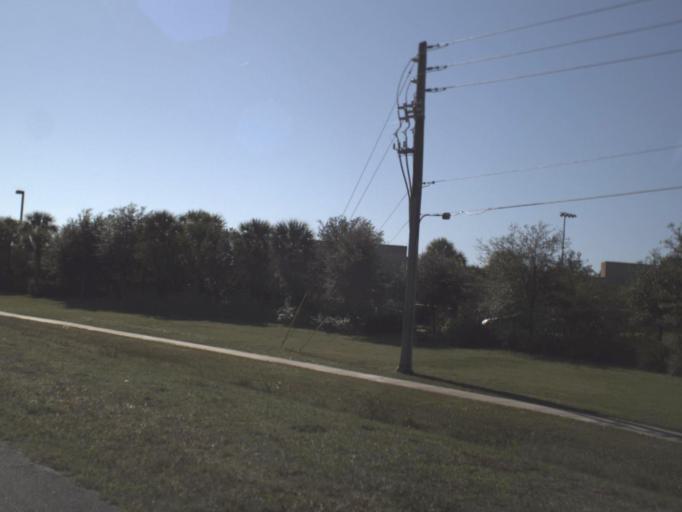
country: US
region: Florida
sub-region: Volusia County
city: Daytona Beach
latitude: 29.1680
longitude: -81.0788
